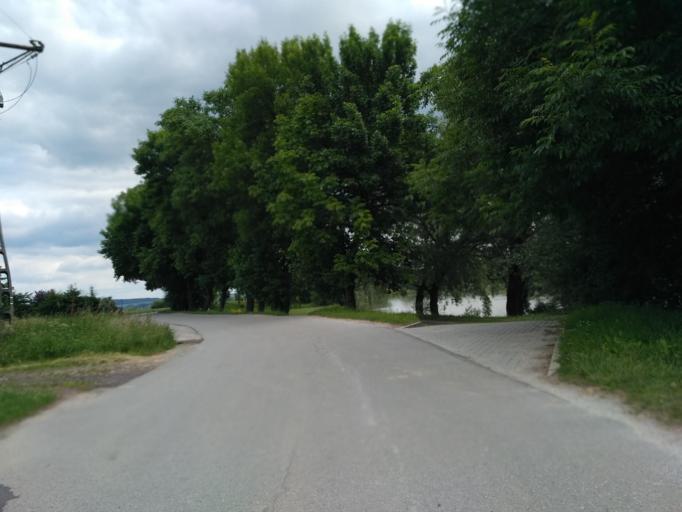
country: PL
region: Subcarpathian Voivodeship
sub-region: Powiat rzeszowski
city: Dynow
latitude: 49.8061
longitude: 22.2428
